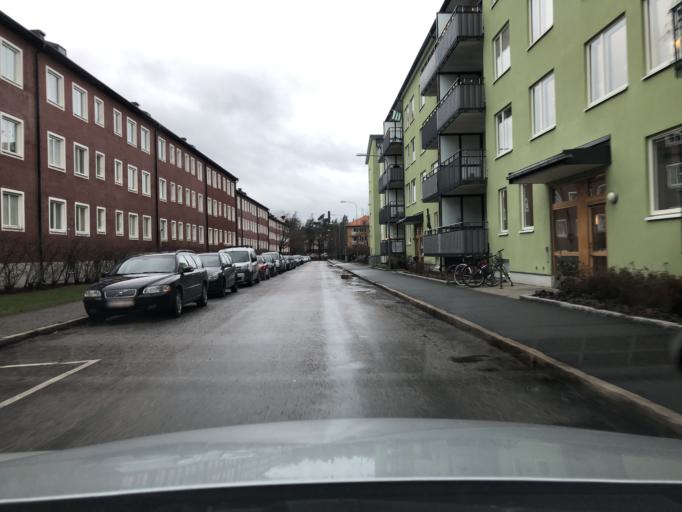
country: SE
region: Stockholm
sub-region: Stockholms Kommun
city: Arsta
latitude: 59.2994
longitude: 18.0464
